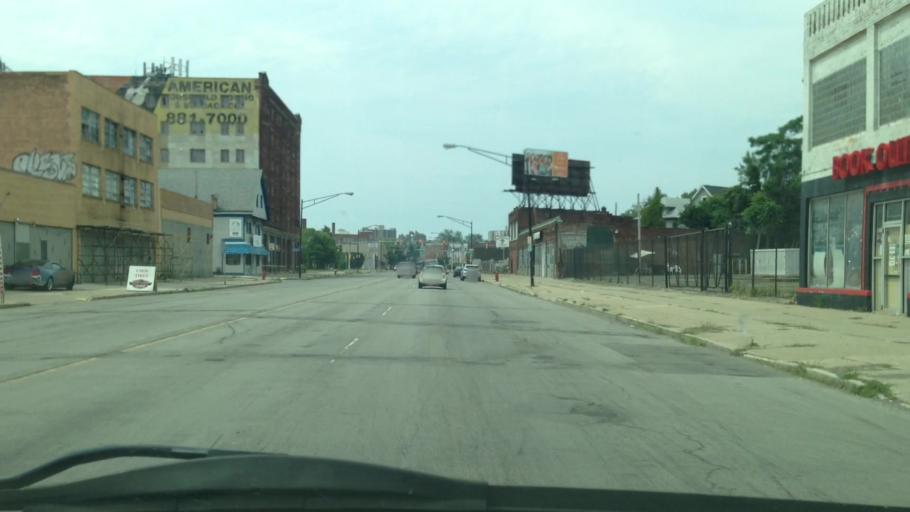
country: US
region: New York
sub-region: Erie County
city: Buffalo
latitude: 42.9190
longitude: -78.8607
